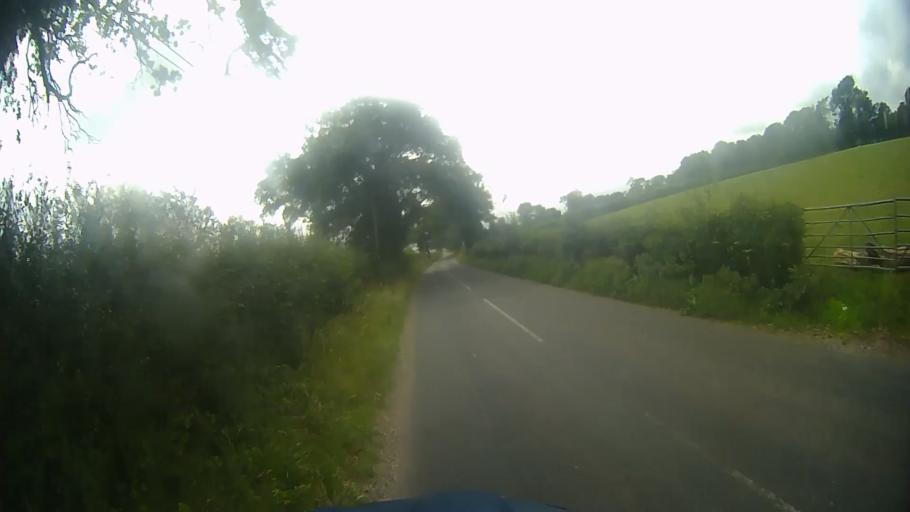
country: GB
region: England
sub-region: Hampshire
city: Overton
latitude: 51.2659
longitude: -1.3108
